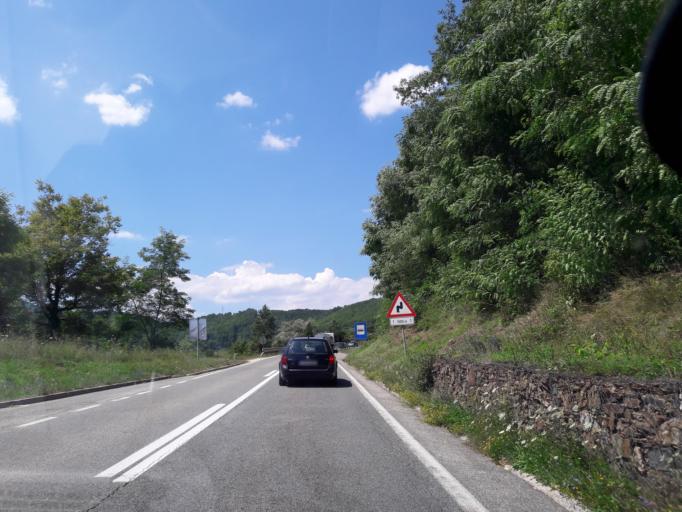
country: BA
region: Republika Srpska
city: Mrkonjic Grad
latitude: 44.3877
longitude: 17.1141
